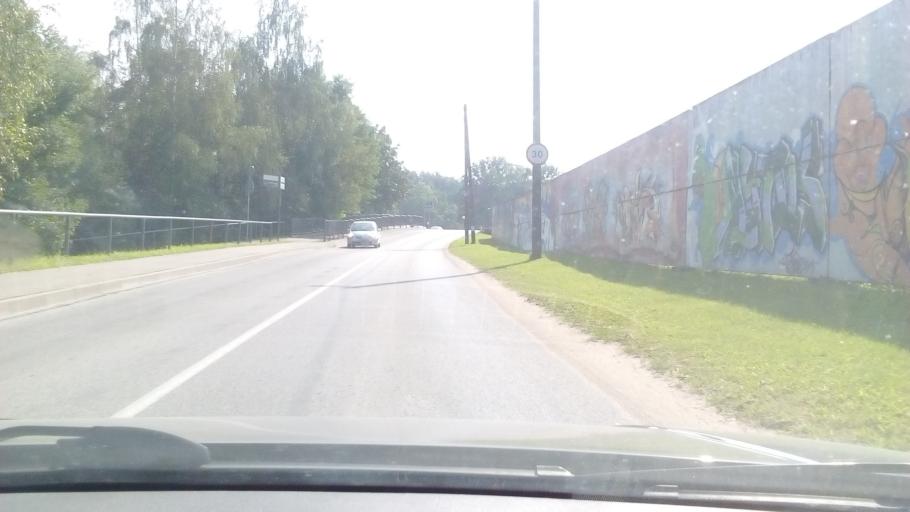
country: LT
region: Alytaus apskritis
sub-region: Alytus
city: Alytus
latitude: 54.3896
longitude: 24.0615
